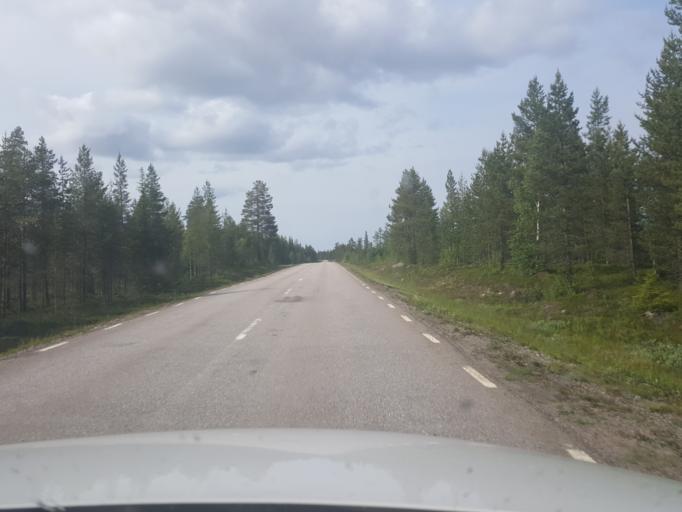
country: SE
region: Norrbotten
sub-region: Arjeplogs Kommun
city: Arjeplog
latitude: 65.6703
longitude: 18.0780
